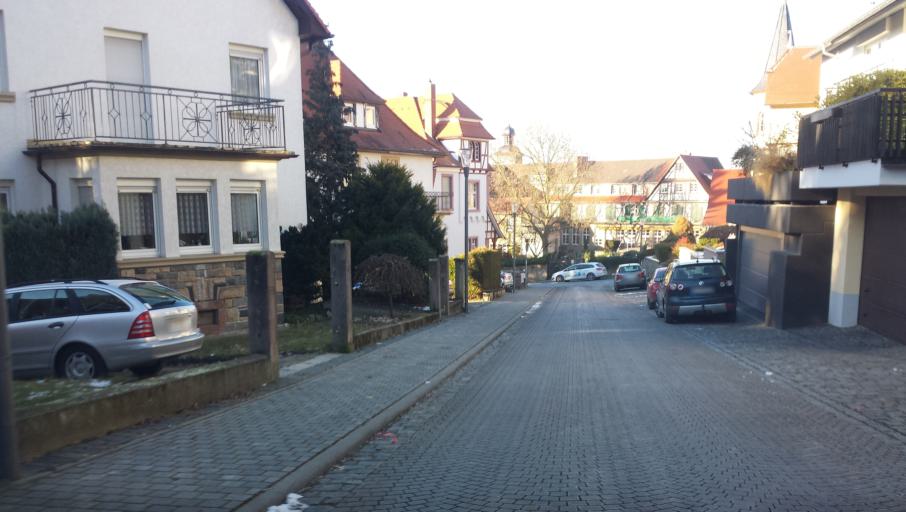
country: DE
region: Hesse
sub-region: Regierungsbezirk Darmstadt
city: Heppenheim an der Bergstrasse
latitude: 49.6404
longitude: 8.6469
